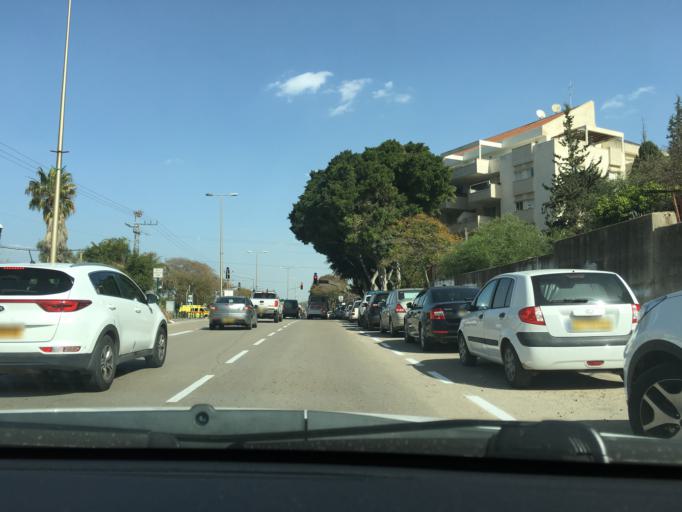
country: IL
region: Central District
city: Kfar Saba
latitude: 32.1800
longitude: 34.8966
